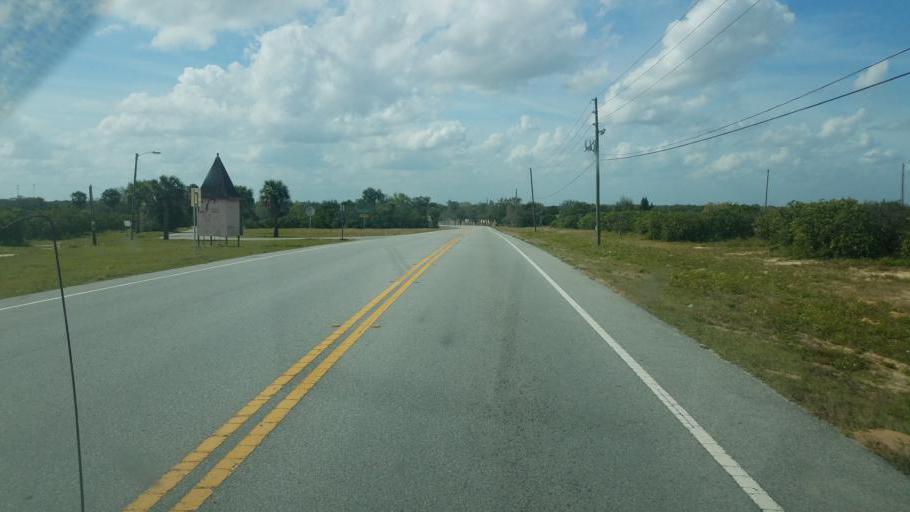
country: US
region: Florida
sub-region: Polk County
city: Lake Wales
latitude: 27.9599
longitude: -81.5960
